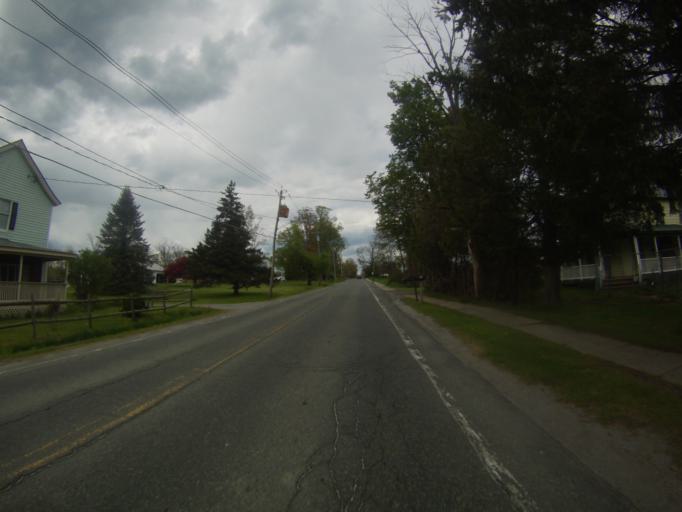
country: US
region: New York
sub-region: Essex County
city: Mineville
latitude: 44.0492
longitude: -73.5067
